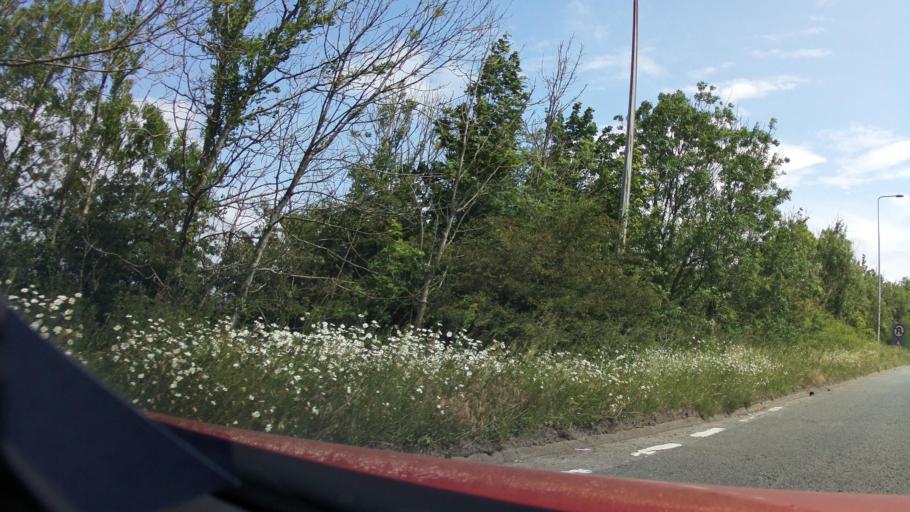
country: GB
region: Wales
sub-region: Vale of Glamorgan
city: Cowbridge
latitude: 51.4584
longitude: -3.4199
